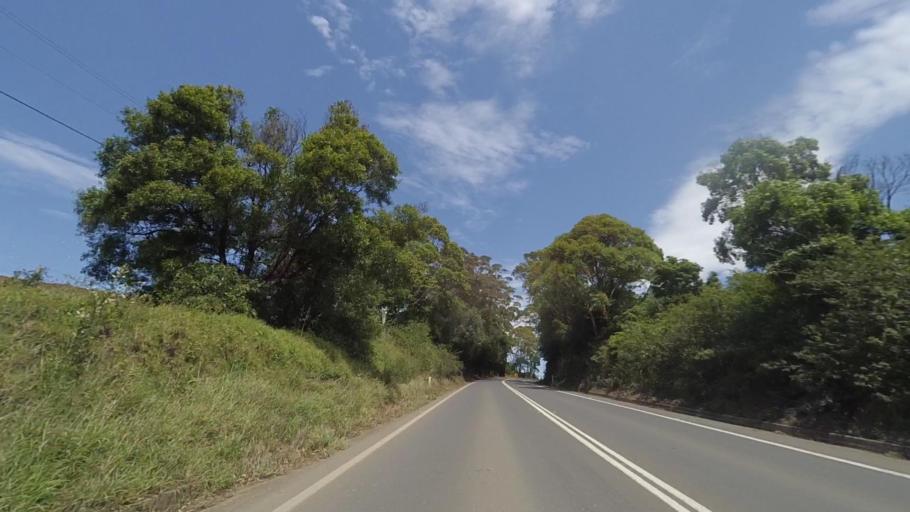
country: AU
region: New South Wales
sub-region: Shoalhaven Shire
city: Berry
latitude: -34.7561
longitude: 150.7485
